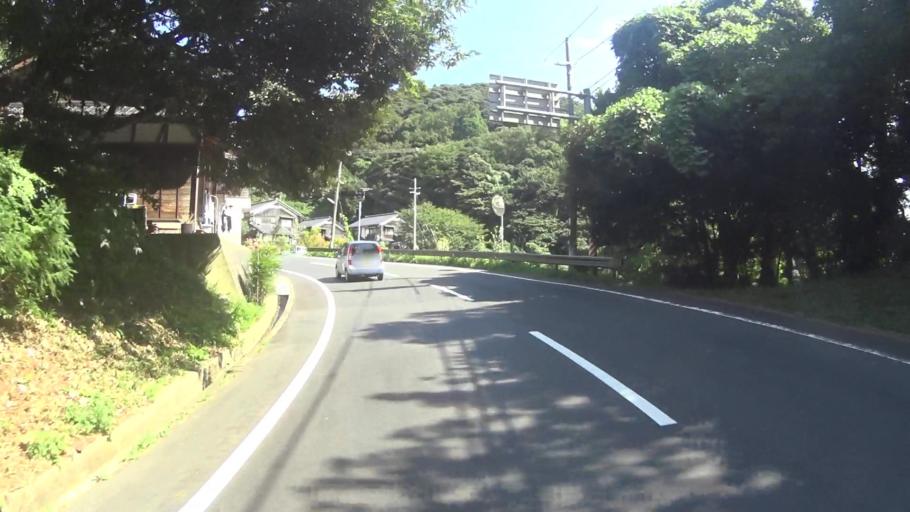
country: JP
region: Kyoto
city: Miyazu
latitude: 35.6775
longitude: 135.2882
